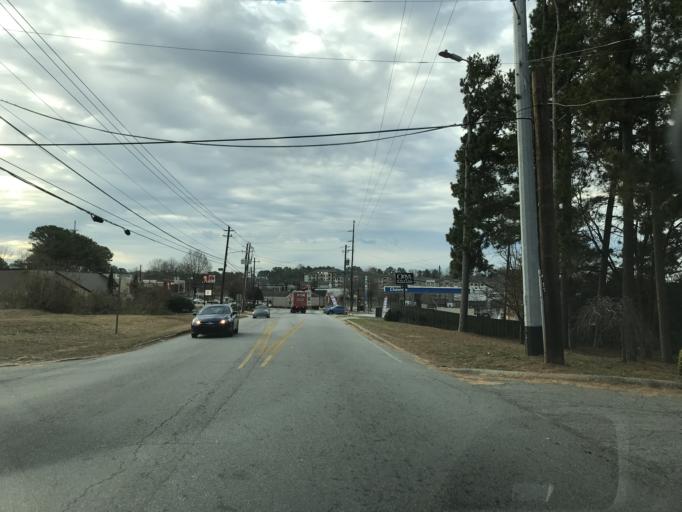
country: US
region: Georgia
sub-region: DeKalb County
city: Doraville
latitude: 33.8869
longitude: -84.2485
